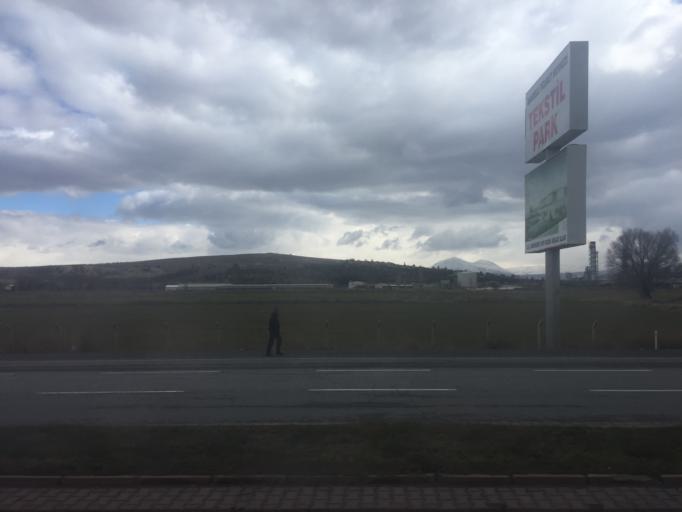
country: TR
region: Kayseri
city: Melikgazi
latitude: 38.7561
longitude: 35.4093
